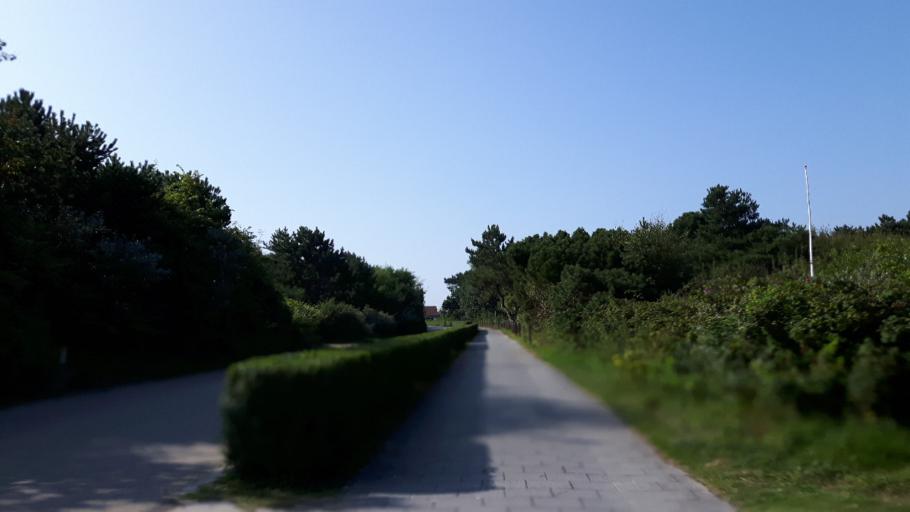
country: NL
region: Friesland
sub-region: Gemeente Ameland
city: Nes
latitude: 53.4577
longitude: 5.8056
